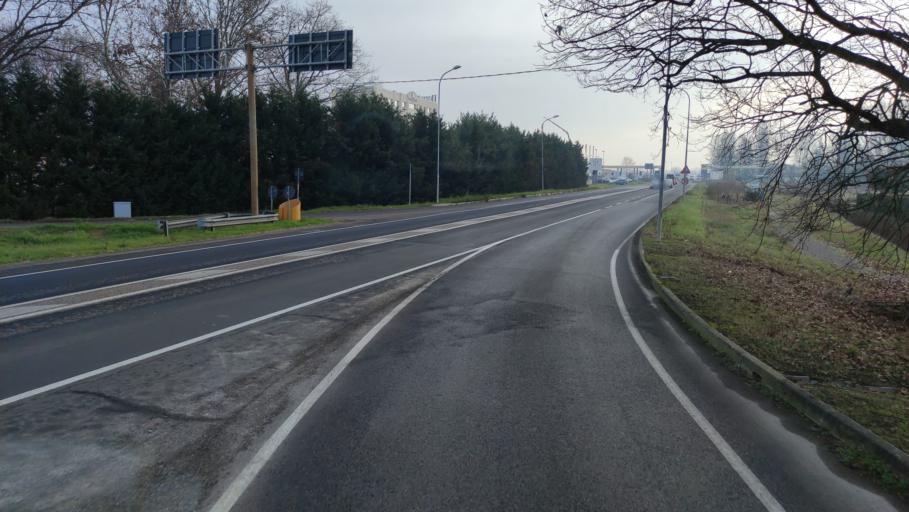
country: IT
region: Emilia-Romagna
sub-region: Provincia di Bologna
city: Castel Maggiore
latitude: 44.5943
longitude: 11.3807
